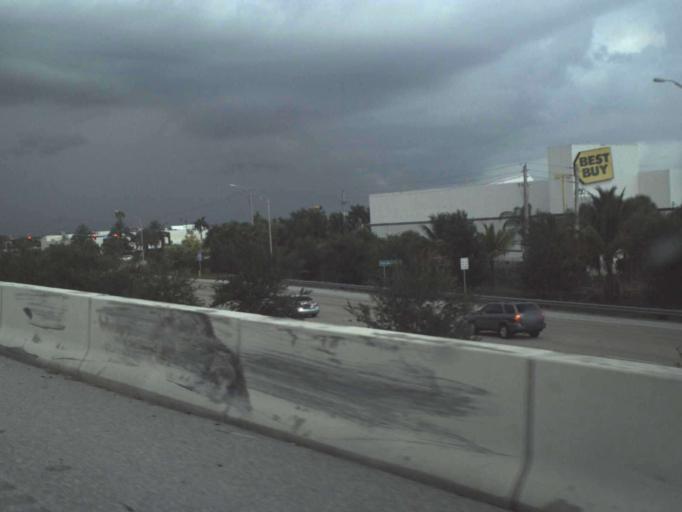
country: US
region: Florida
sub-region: Palm Beach County
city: Schall Circle
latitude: 26.7176
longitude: -80.0881
